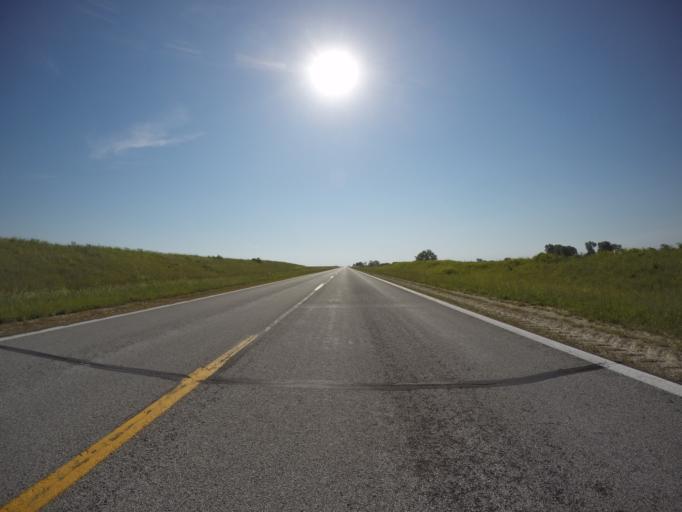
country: US
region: Nebraska
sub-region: Pawnee County
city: Pawnee City
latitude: 40.0447
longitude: -96.3621
